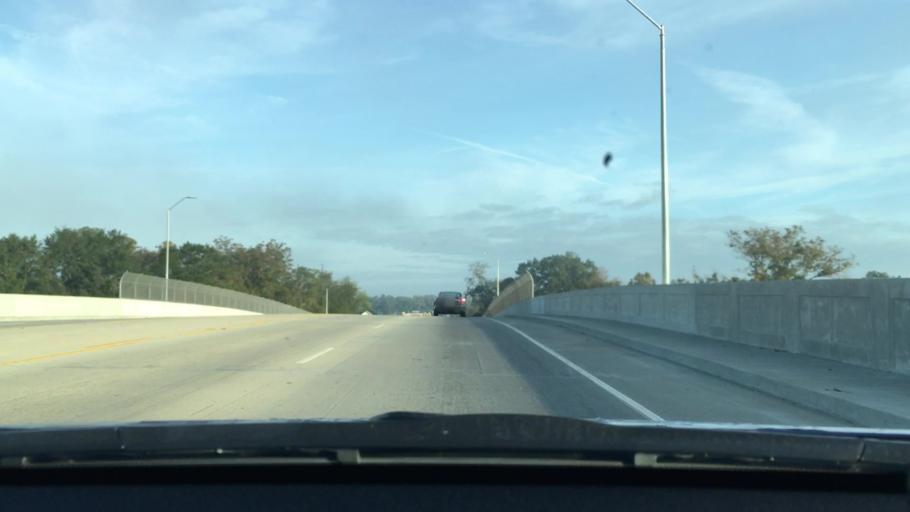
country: US
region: South Carolina
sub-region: Sumter County
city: Sumter
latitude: 33.9166
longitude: -80.3362
